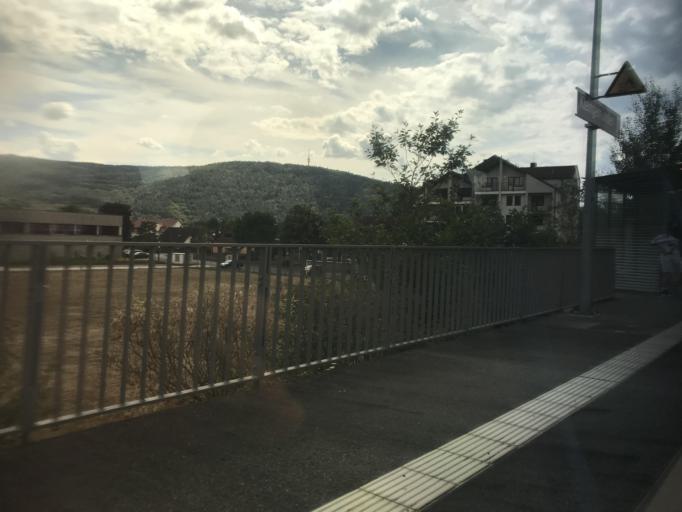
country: DE
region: Bavaria
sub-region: Regierungsbezirk Unterfranken
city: Gemunden
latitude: 50.0630
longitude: 9.6881
